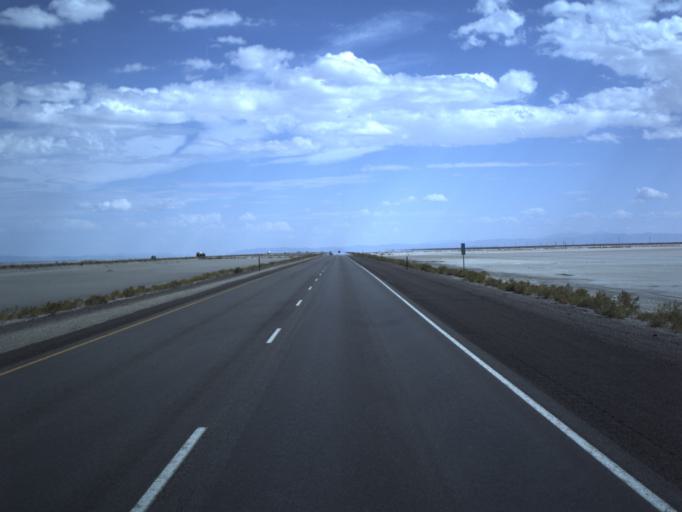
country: US
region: Utah
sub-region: Tooele County
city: Wendover
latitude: 40.7362
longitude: -113.7422
